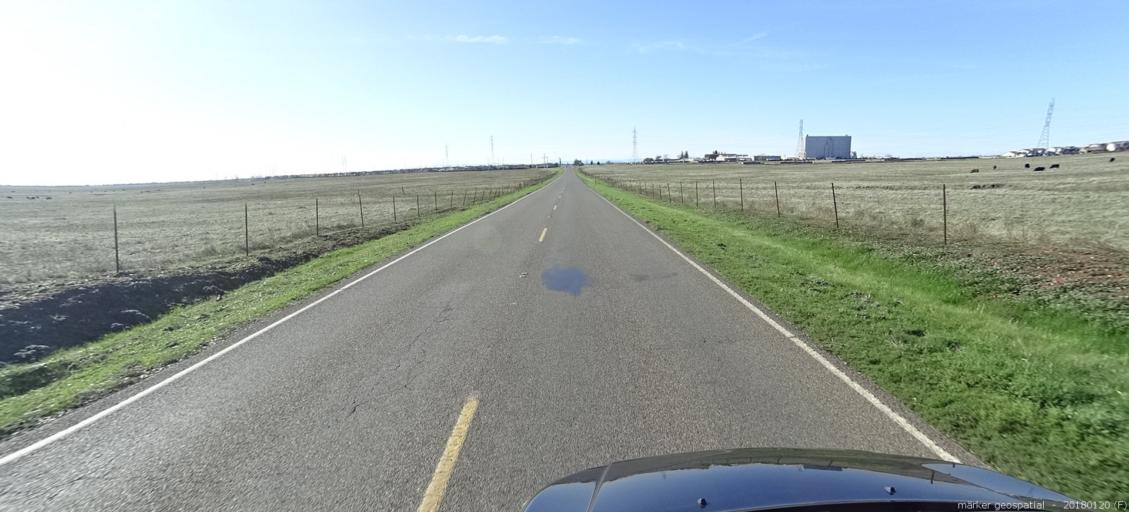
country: US
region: California
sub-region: Sacramento County
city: Gold River
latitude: 38.5592
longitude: -121.1952
